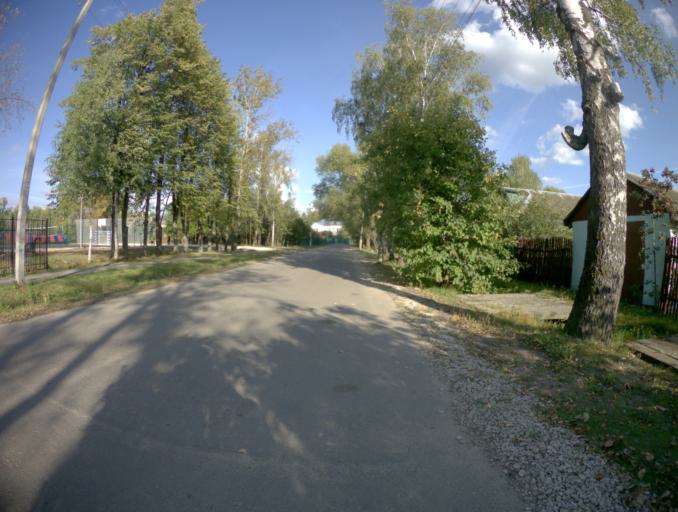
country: RU
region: Vladimir
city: Petushki
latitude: 55.9283
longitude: 39.4620
